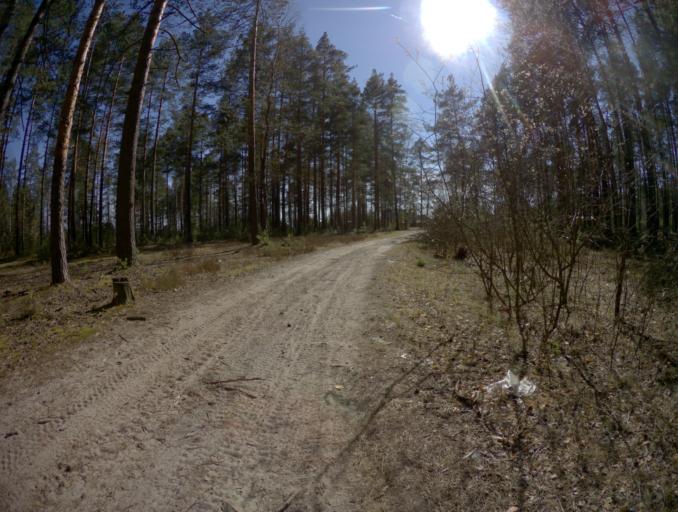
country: RU
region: Vladimir
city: Ivanishchi
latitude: 55.7836
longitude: 40.4271
